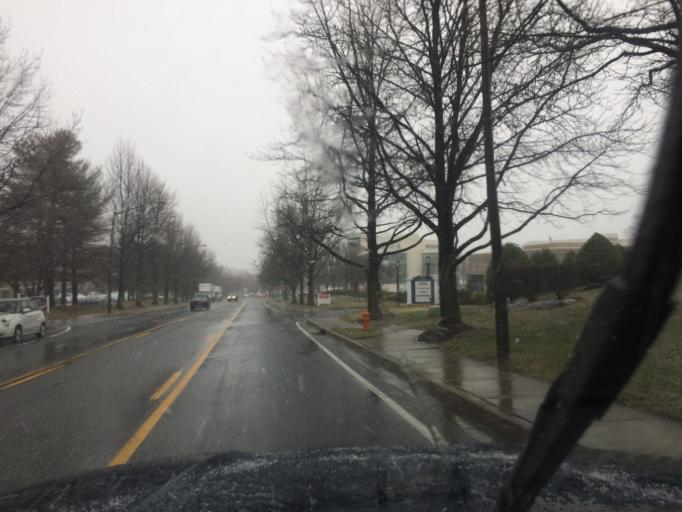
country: US
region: Maryland
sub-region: Howard County
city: Columbia
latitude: 39.2301
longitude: -76.8146
